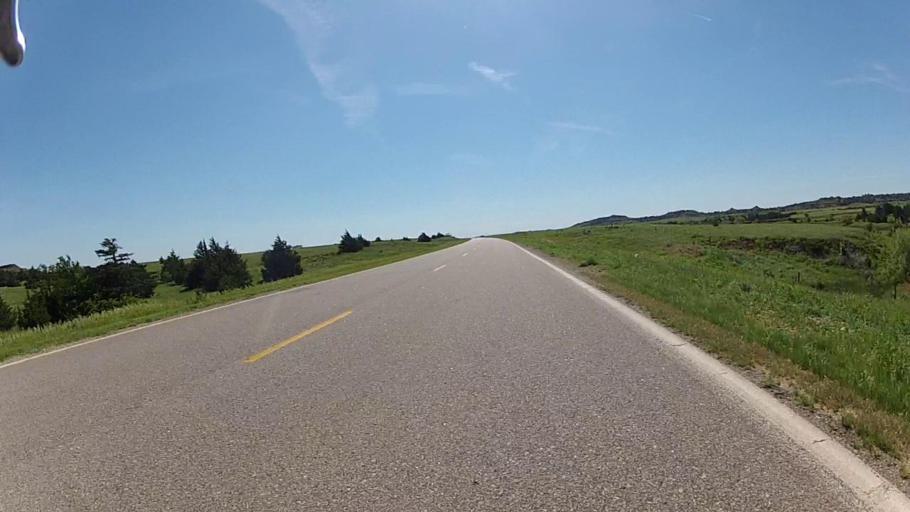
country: US
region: Kansas
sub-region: Barber County
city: Medicine Lodge
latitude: 37.2754
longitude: -98.7270
